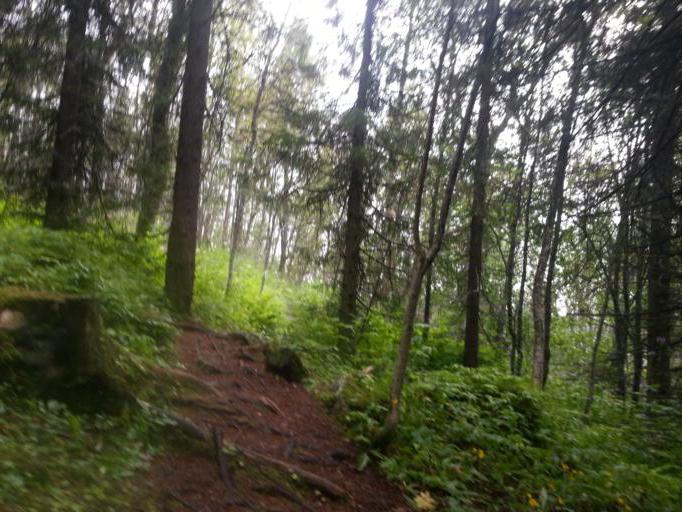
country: NO
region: Troms
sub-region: Tromso
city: Tromso
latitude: 69.6363
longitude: 18.9060
